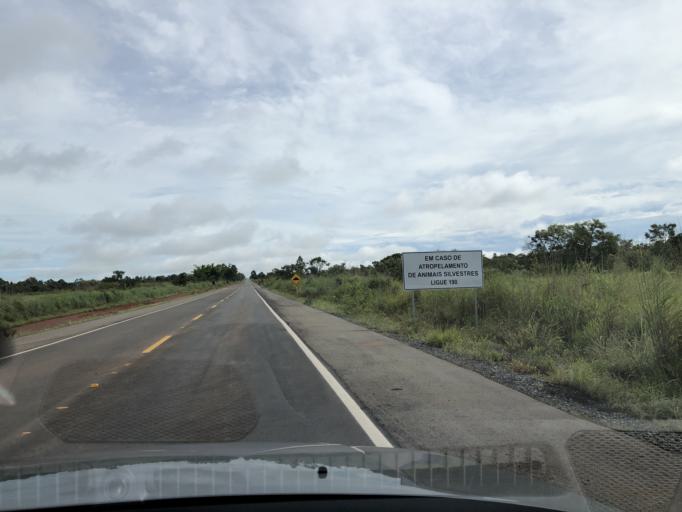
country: BR
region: Federal District
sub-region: Brasilia
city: Brasilia
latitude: -15.6636
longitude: -48.0856
